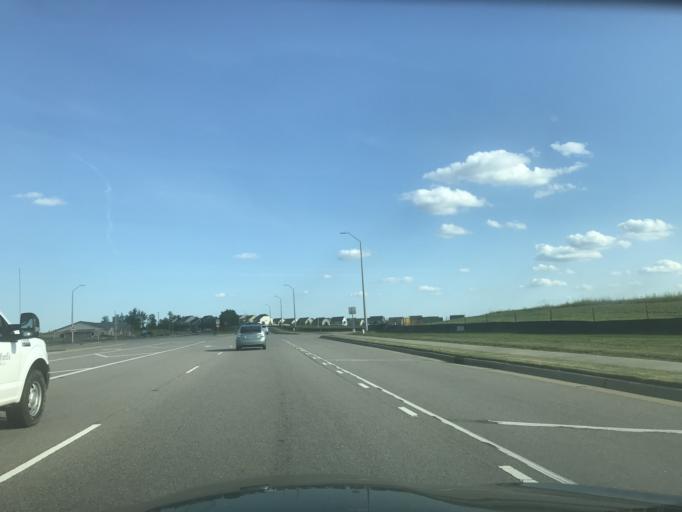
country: US
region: North Carolina
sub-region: Wake County
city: Knightdale
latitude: 35.7771
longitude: -78.4340
